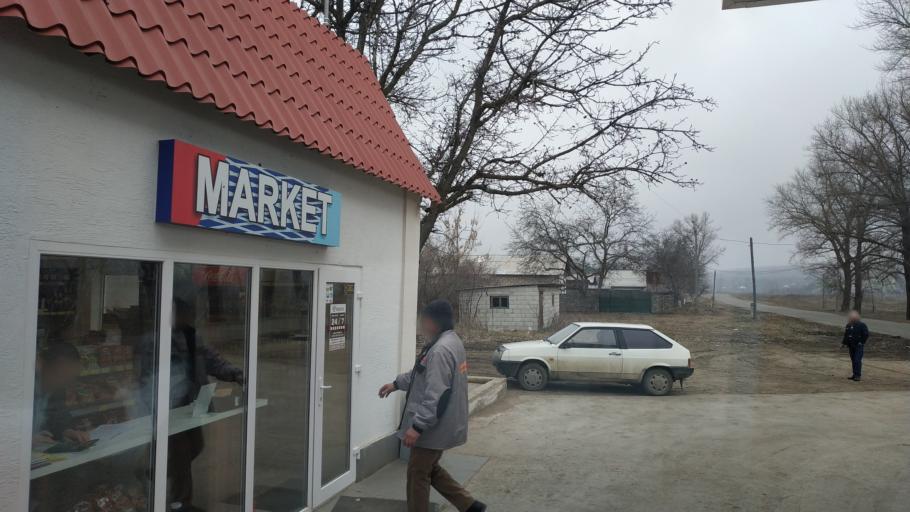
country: MD
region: Hincesti
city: Hincesti
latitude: 46.9720
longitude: 28.4738
